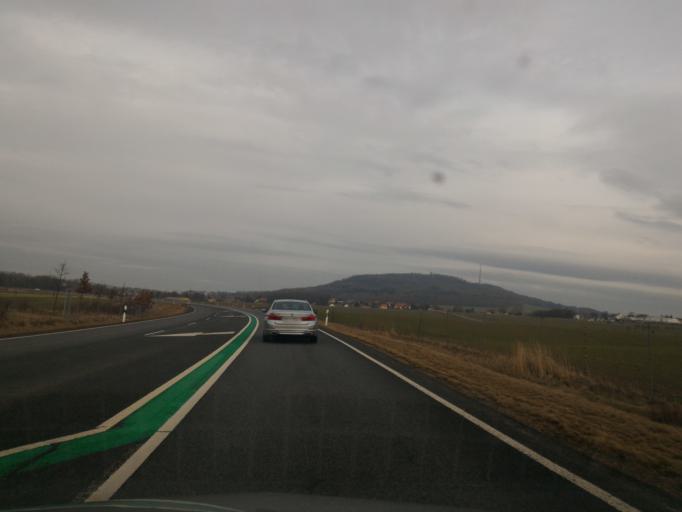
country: DE
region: Saxony
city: Niedercunnersdorf
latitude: 51.0715
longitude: 14.6704
